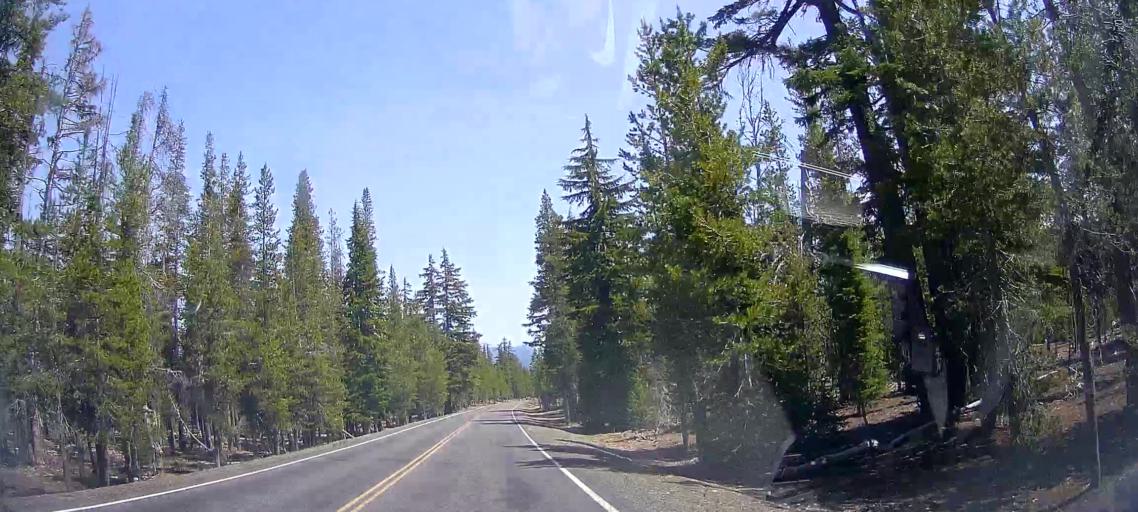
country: US
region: Oregon
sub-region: Jackson County
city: Shady Cove
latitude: 43.0061
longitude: -122.1331
